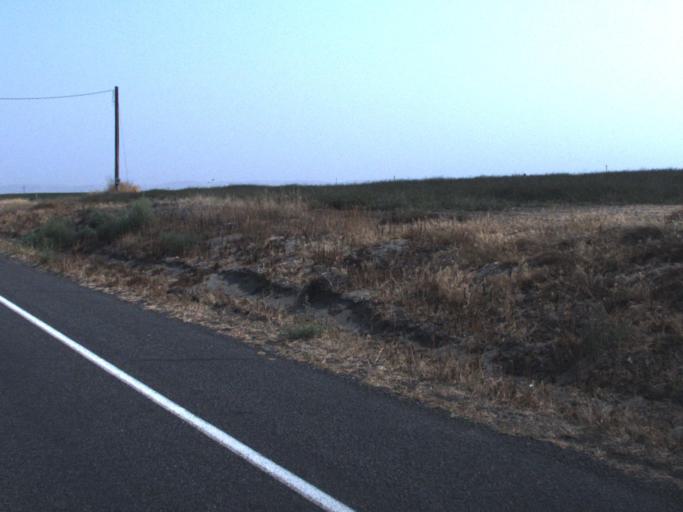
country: US
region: Washington
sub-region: Yakima County
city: Mabton
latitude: 46.2381
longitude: -120.0900
